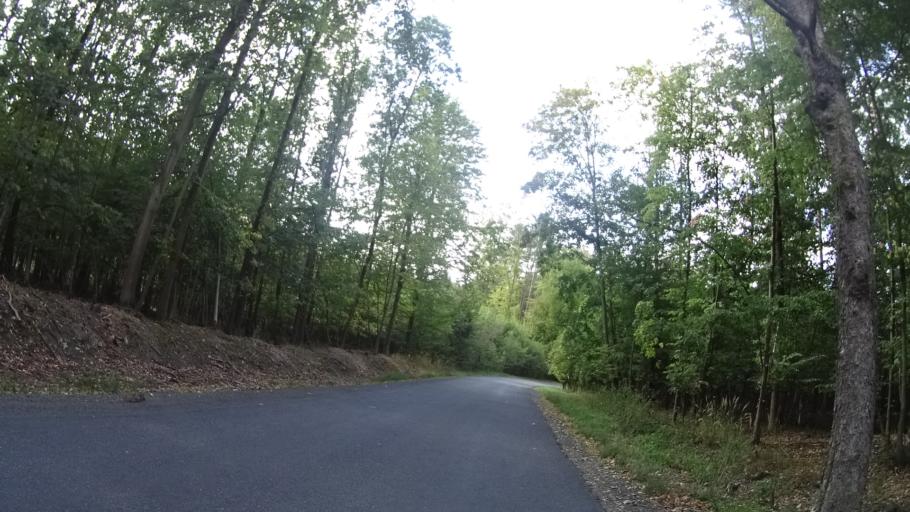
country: CZ
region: Olomoucky
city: Bila Lhota
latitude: 49.7295
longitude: 17.0104
